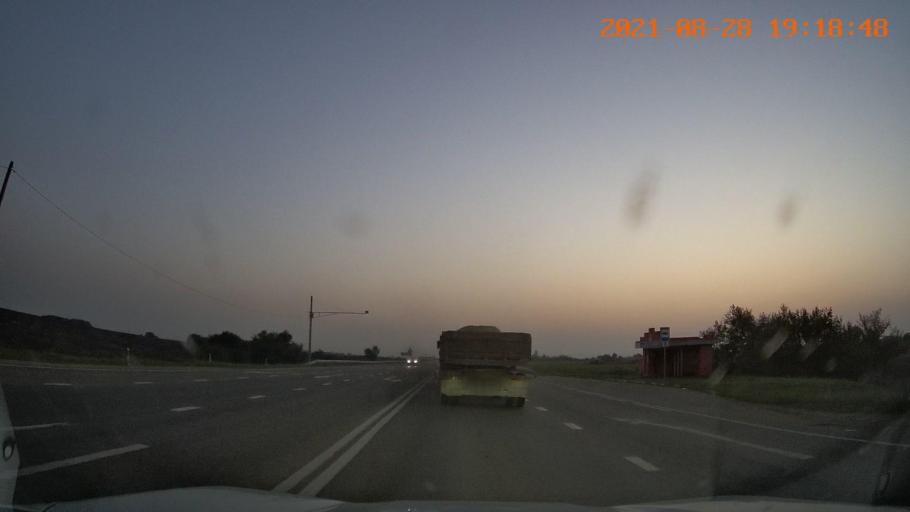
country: RU
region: Krasnodarskiy
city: Ryazanskaya
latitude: 44.8925
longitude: 39.5226
